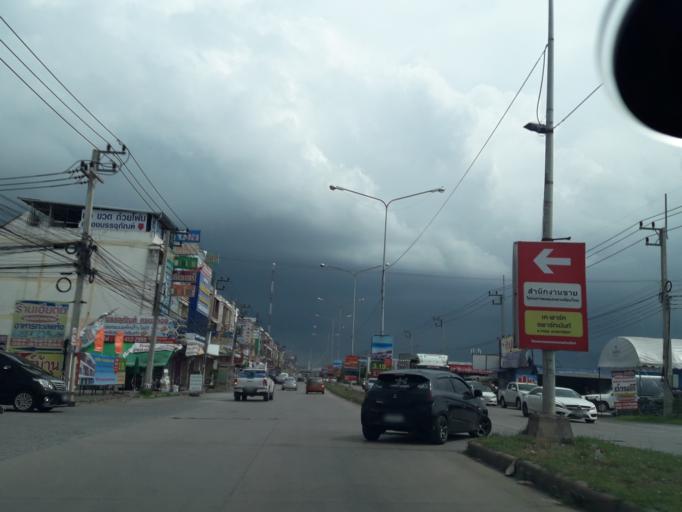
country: TH
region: Pathum Thani
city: Khlong Luang
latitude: 14.0735
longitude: 100.6340
